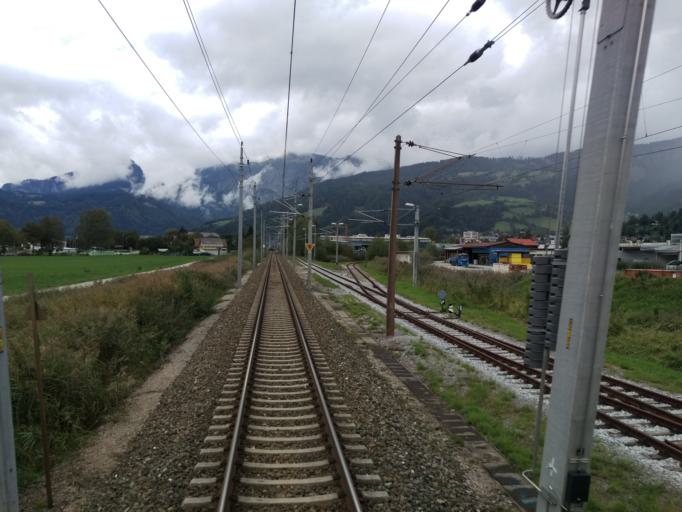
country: AT
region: Styria
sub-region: Politischer Bezirk Liezen
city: Liezen
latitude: 47.5578
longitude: 14.2515
